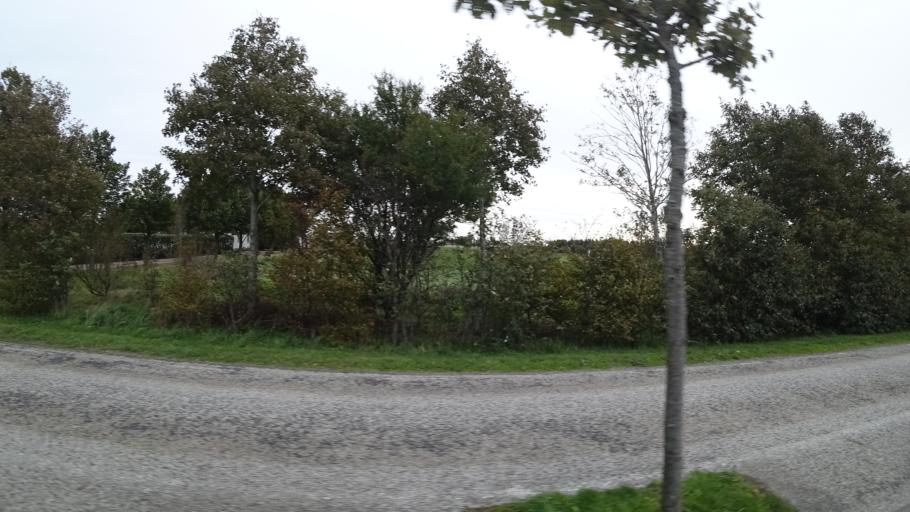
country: SE
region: Skane
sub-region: Kavlinge Kommun
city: Loddekopinge
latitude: 55.7713
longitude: 13.0114
